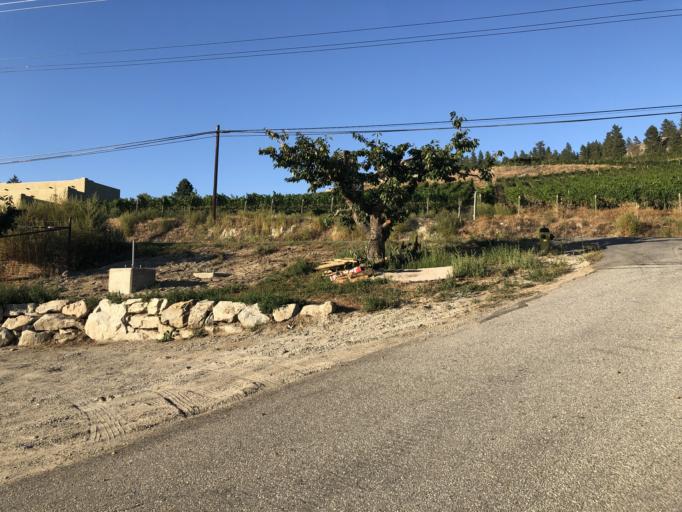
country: CA
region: British Columbia
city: Penticton
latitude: 49.5421
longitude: -119.5674
